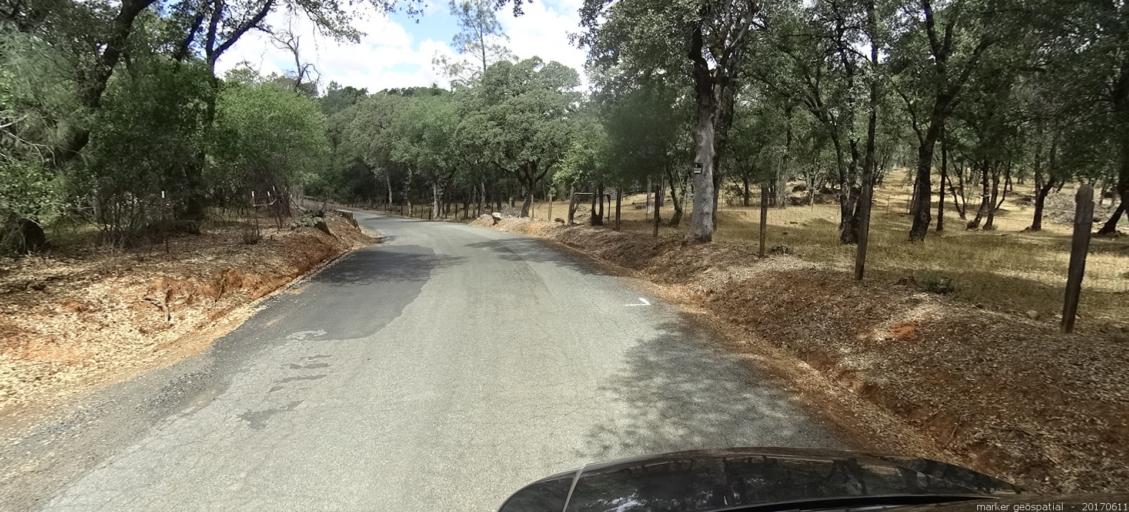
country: US
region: California
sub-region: Butte County
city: Oroville
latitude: 39.5980
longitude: -121.5331
